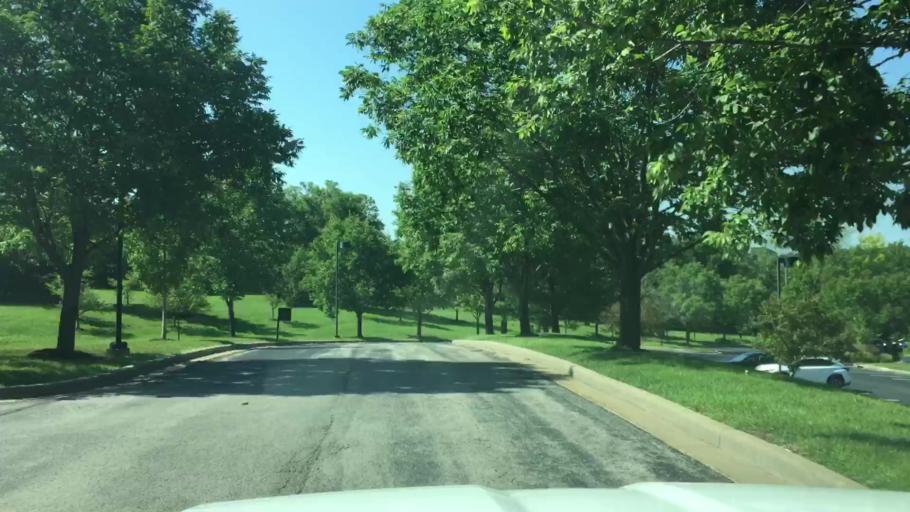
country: US
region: Missouri
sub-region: Saint Louis County
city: Manchester
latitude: 38.6398
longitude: -90.5064
